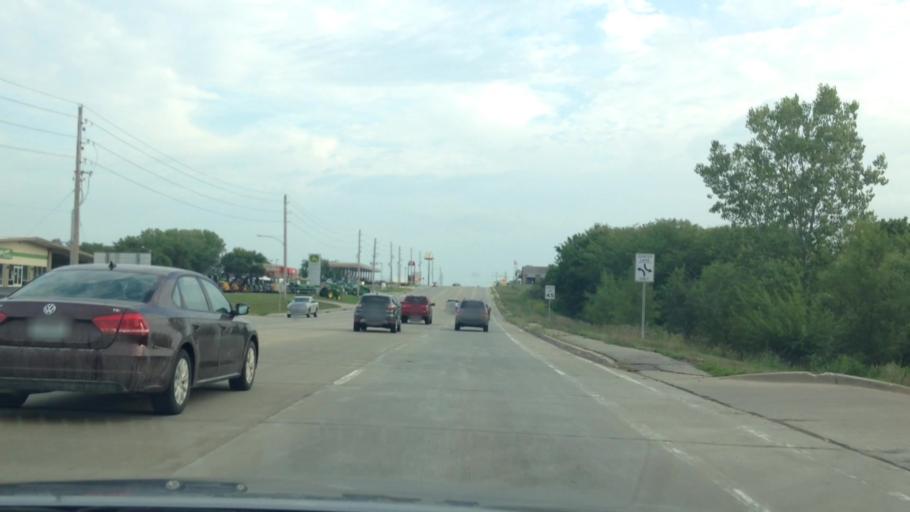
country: US
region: Missouri
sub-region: Clay County
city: Smithville
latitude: 39.3677
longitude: -94.5835
